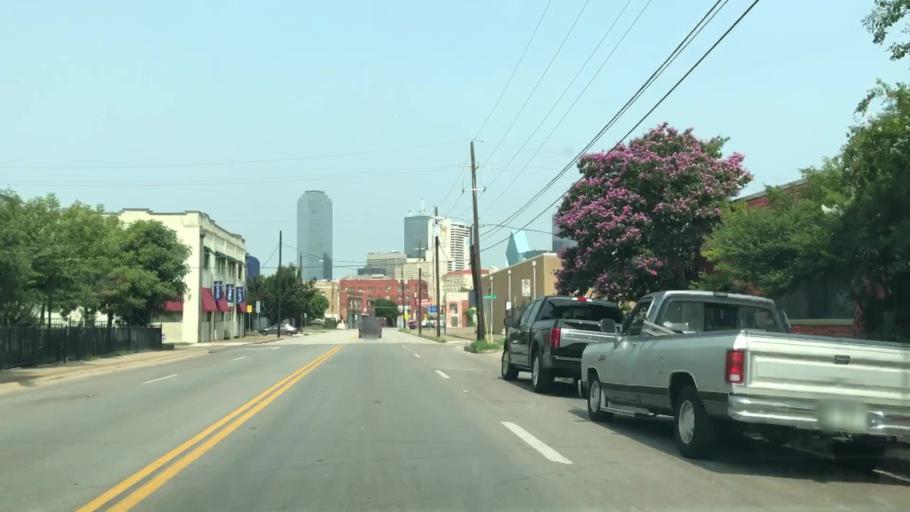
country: US
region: Texas
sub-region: Dallas County
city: Dallas
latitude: 32.7699
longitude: -96.7871
